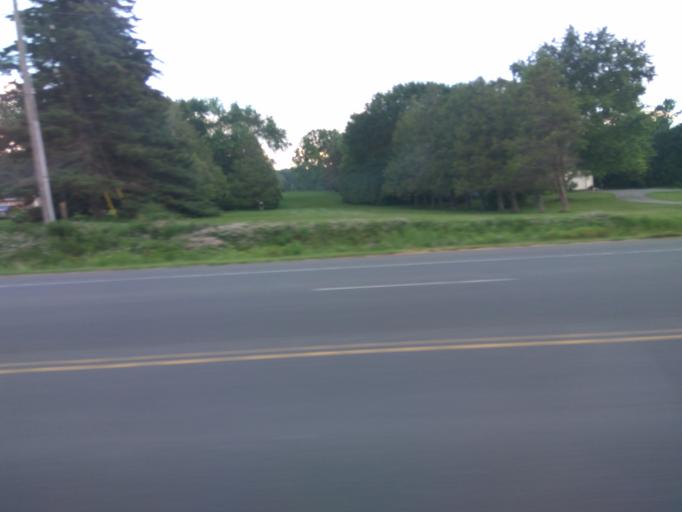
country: CA
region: Ontario
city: Stratford
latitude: 43.3704
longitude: -80.9233
